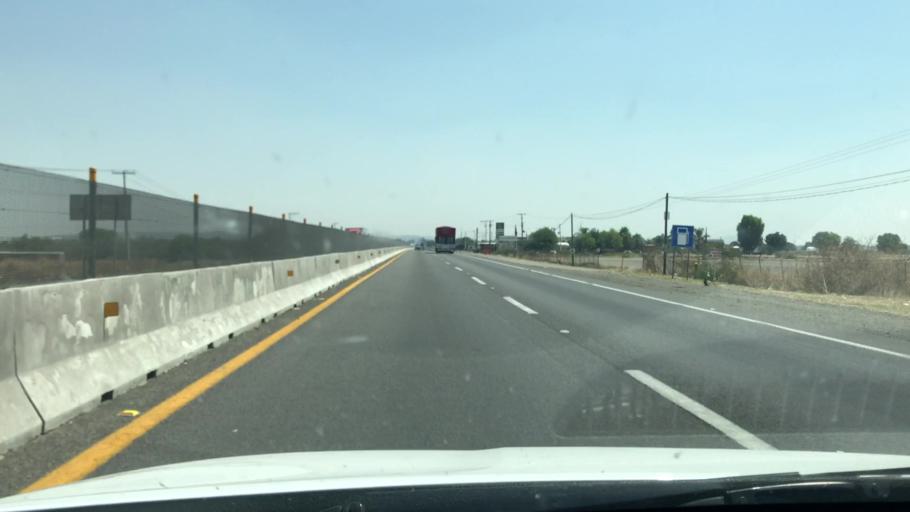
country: MX
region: Guanajuato
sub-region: Abasolo
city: San Bernardo Pena Blanca
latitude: 20.4727
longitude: -101.5025
